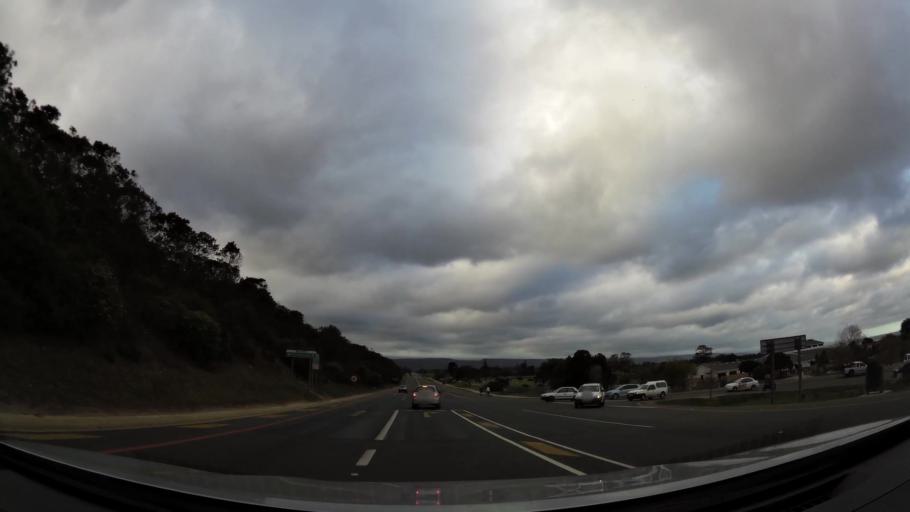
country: ZA
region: Western Cape
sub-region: Eden District Municipality
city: Plettenberg Bay
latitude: -34.0404
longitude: 23.3697
